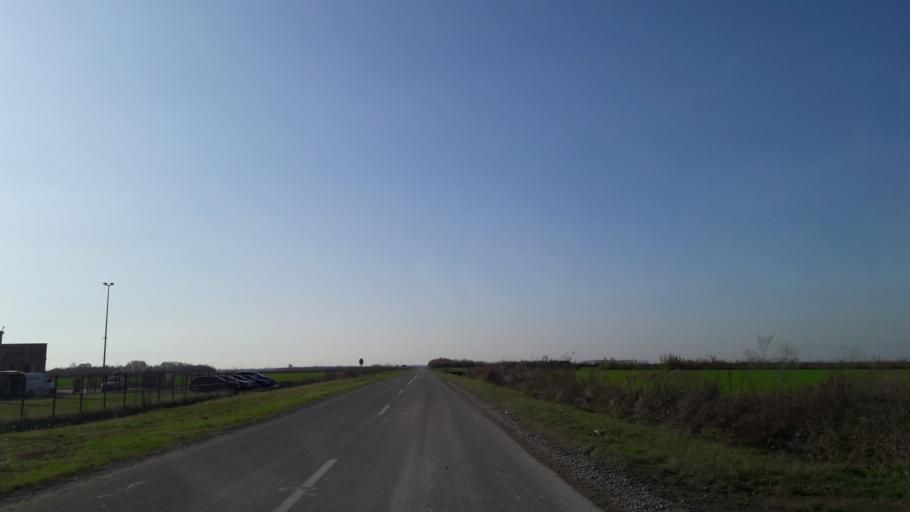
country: HR
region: Osjecko-Baranjska
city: Tenja
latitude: 45.4830
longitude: 18.7178
